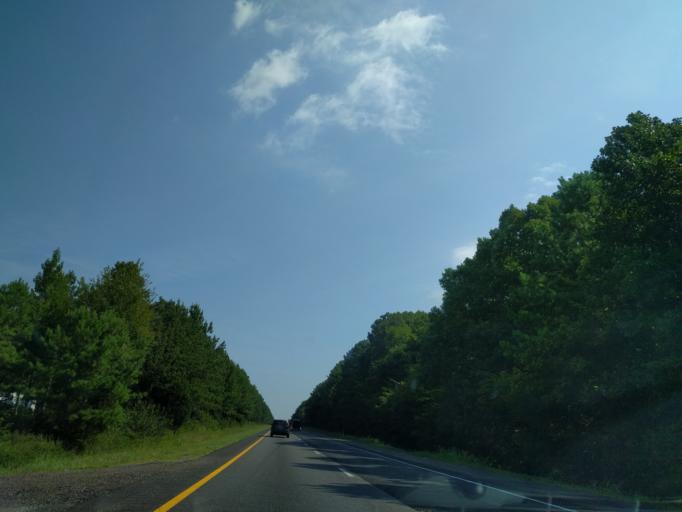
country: US
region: Tennessee
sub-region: Robertson County
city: Cross Plains
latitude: 36.5491
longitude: -86.6326
